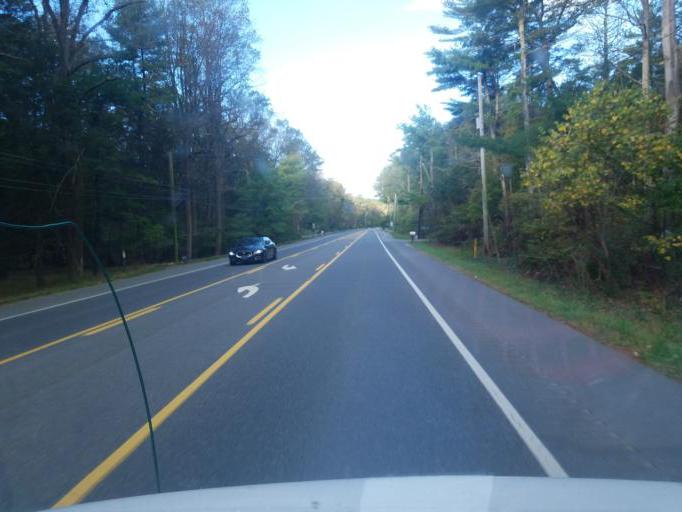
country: US
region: Pennsylvania
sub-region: Franklin County
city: Fayetteville
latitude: 39.8997
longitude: -77.4461
